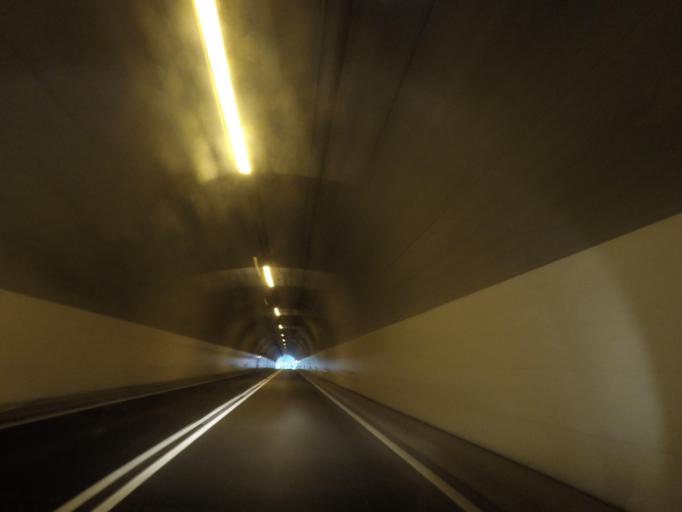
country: PT
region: Madeira
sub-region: Santana
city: Santana
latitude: 32.8095
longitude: -16.8776
